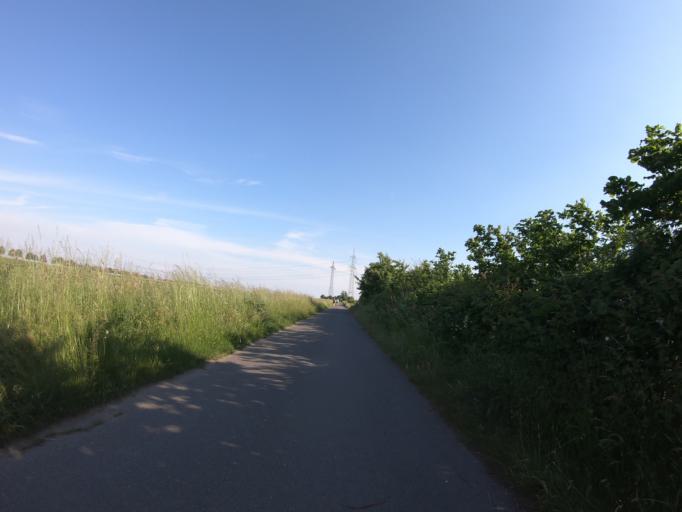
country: DE
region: Lower Saxony
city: Meine
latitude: 52.3739
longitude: 10.5434
